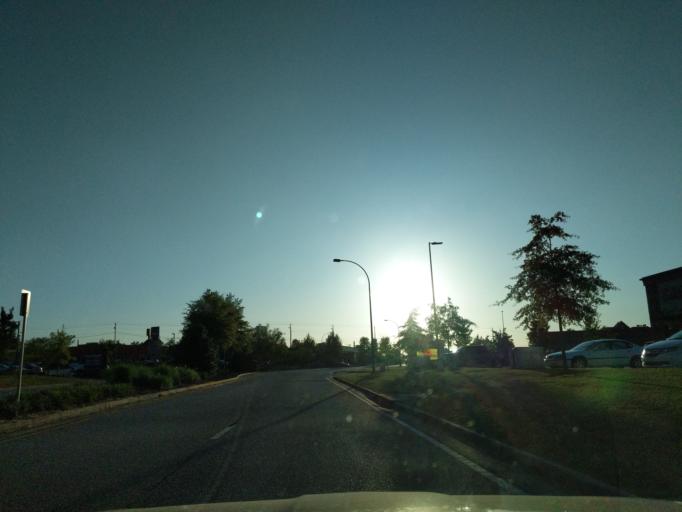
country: US
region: Georgia
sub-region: Columbia County
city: Grovetown
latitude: 33.4793
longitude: -82.1946
